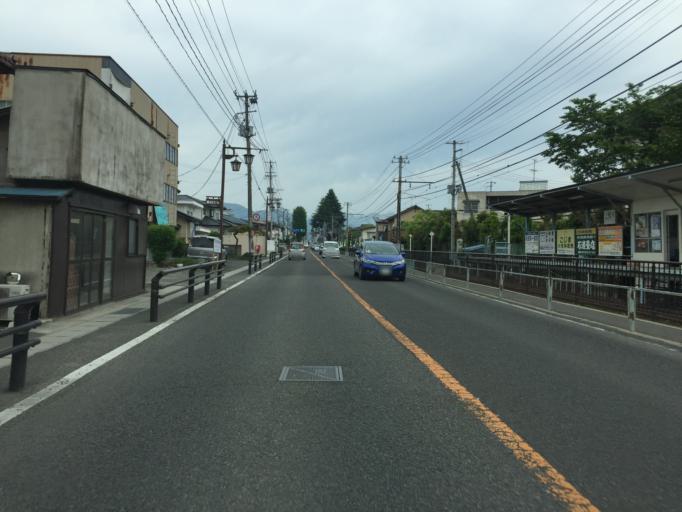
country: JP
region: Fukushima
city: Fukushima-shi
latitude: 37.7834
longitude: 140.4410
